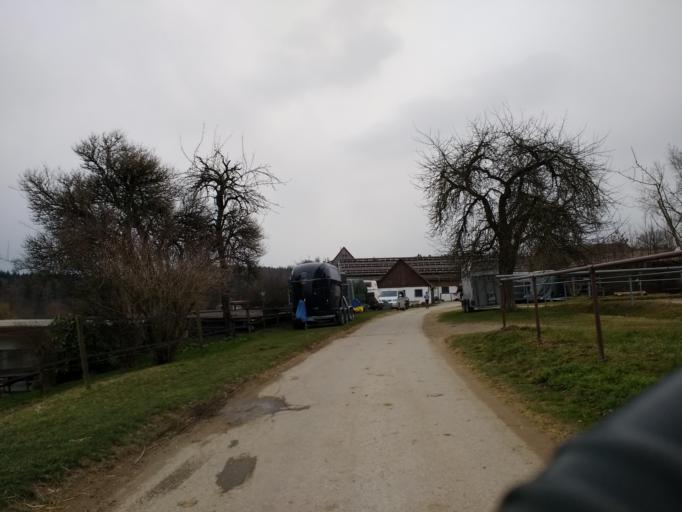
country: DE
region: Baden-Wuerttemberg
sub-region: Tuebingen Region
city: Uberlingen
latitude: 47.7418
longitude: 9.1326
